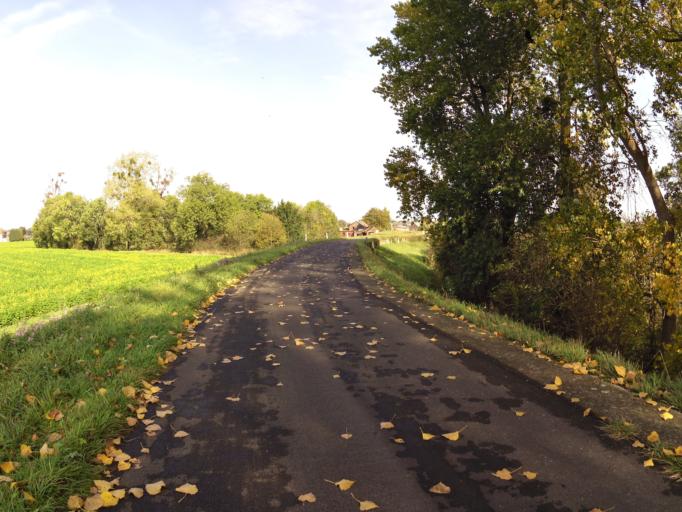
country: NL
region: Limburg
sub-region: Gemeente Stein
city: Elsloo
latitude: 50.9427
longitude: 5.7413
